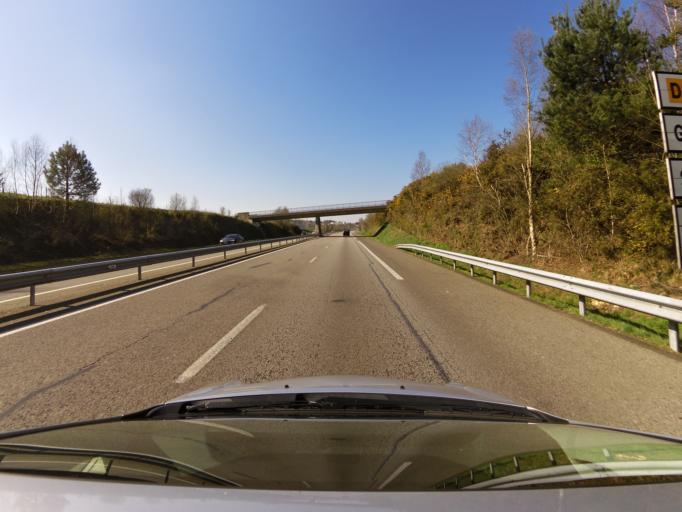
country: FR
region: Brittany
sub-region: Departement du Morbihan
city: Guer
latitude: 47.9382
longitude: -2.1126
